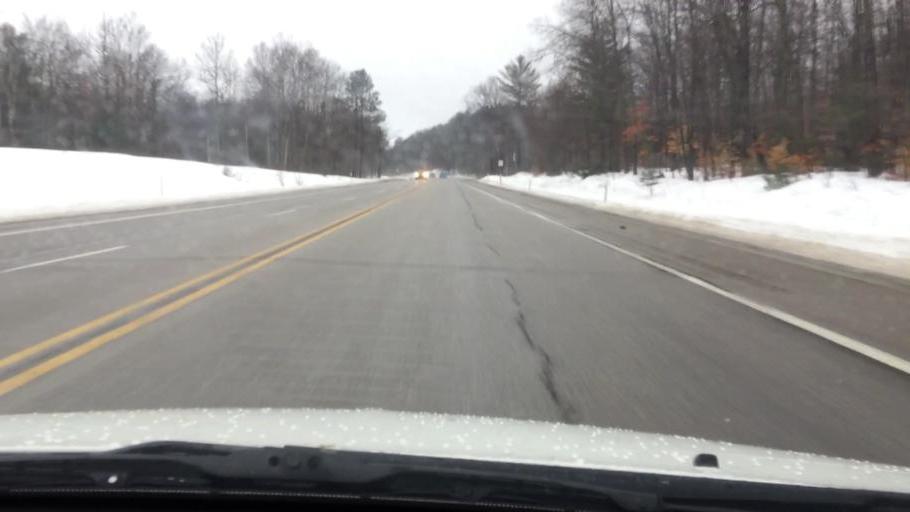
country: US
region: Michigan
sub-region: Kalkaska County
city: Kalkaska
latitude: 44.6086
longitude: -85.3175
